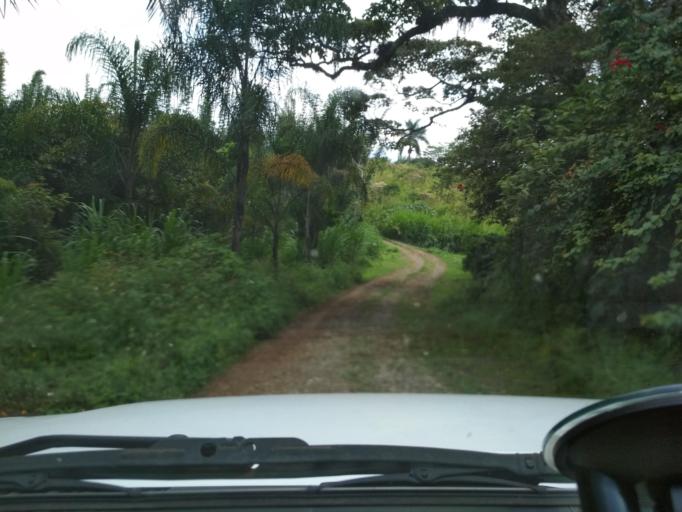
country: MX
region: Veracruz
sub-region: Fortin
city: Monte Salas
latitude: 18.9307
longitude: -97.0158
